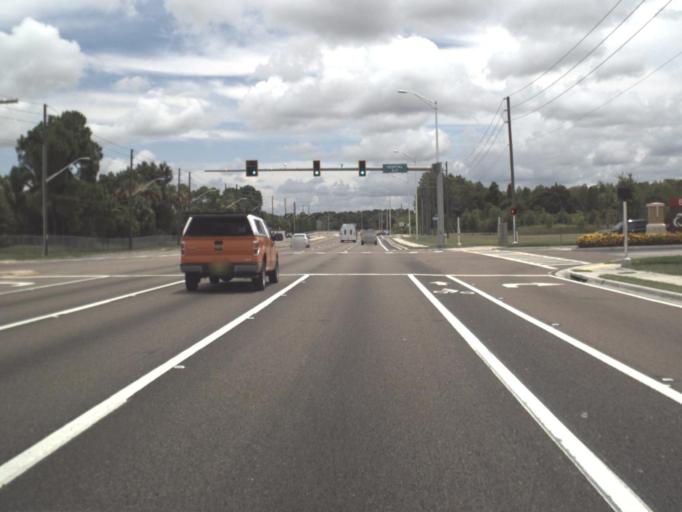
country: US
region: Florida
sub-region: Pasco County
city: Trinity
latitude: 28.2060
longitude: -82.6608
